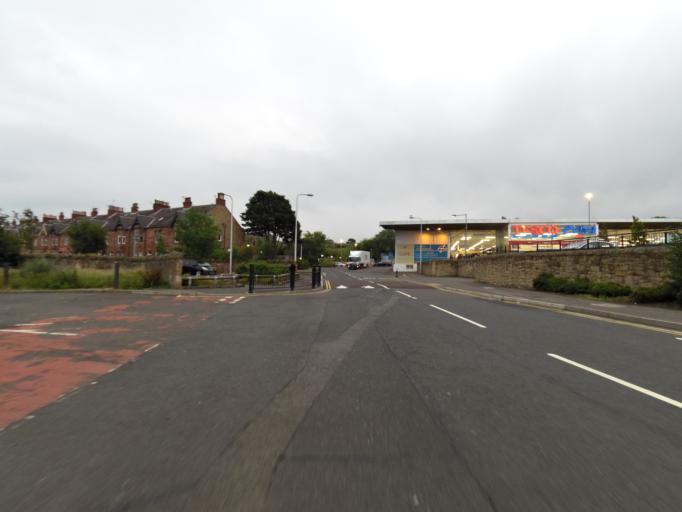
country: GB
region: Scotland
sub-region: East Lothian
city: Musselburgh
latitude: 55.9397
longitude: -3.0549
